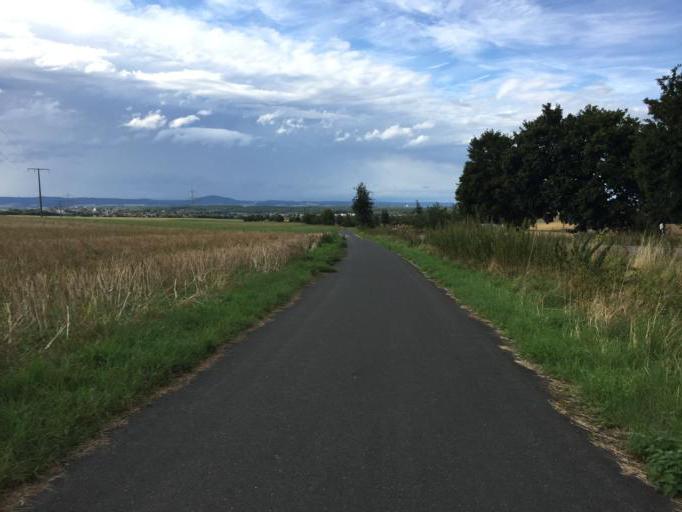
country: DE
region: Hesse
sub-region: Regierungsbezirk Giessen
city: Langgons
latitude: 50.5074
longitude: 8.6825
